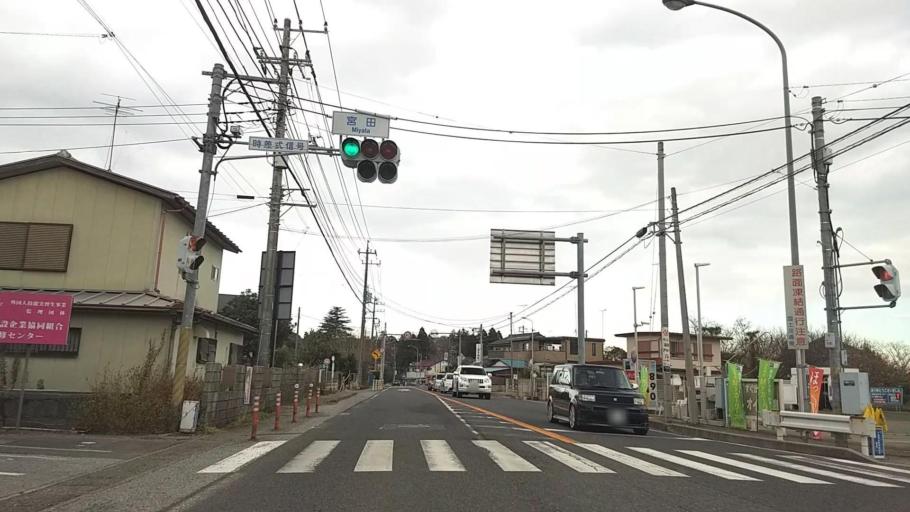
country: JP
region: Chiba
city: Yotsukaido
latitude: 35.5934
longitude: 140.2222
